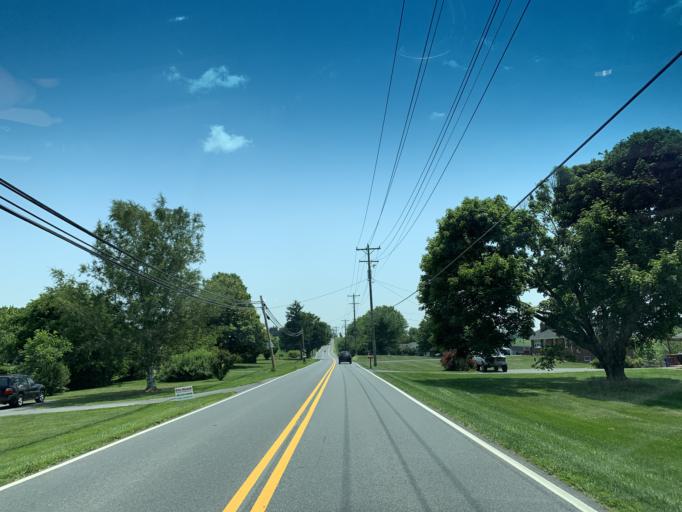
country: US
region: Maryland
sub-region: Frederick County
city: Green Valley
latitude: 39.3576
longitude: -77.2697
